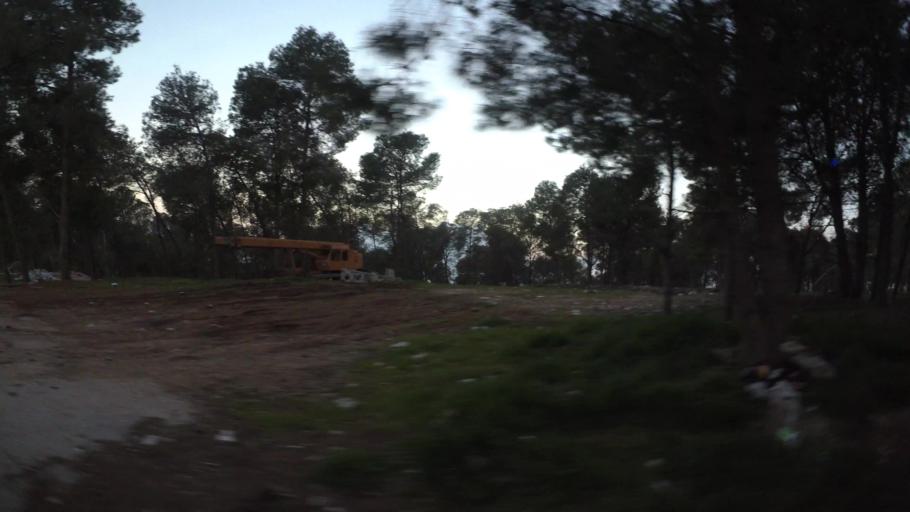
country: JO
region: Amman
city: Al Bunayyat ash Shamaliyah
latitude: 31.8886
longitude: 35.9209
